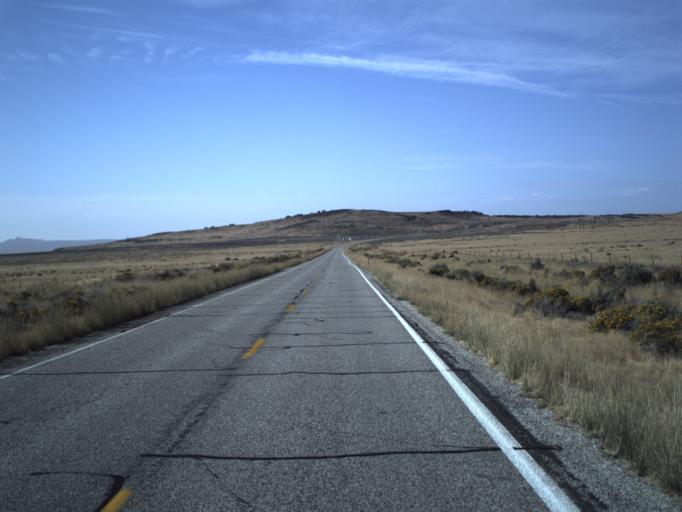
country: US
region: Idaho
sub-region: Minidoka County
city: Rupert
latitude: 41.8480
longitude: -113.1360
